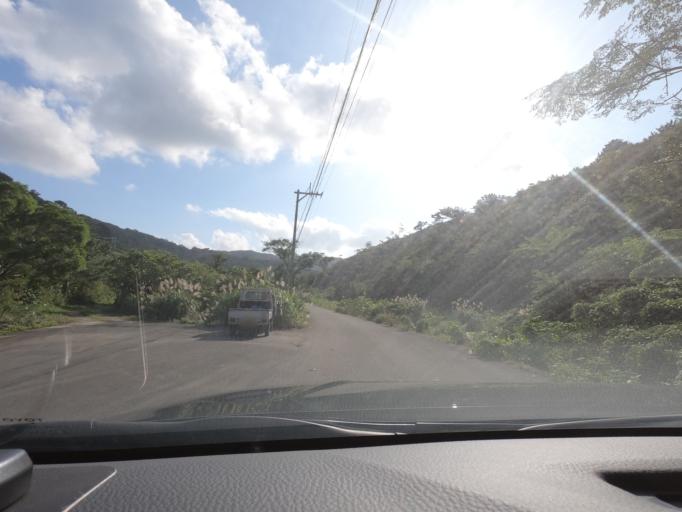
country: JP
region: Okinawa
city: Nago
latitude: 26.7655
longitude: 128.2107
